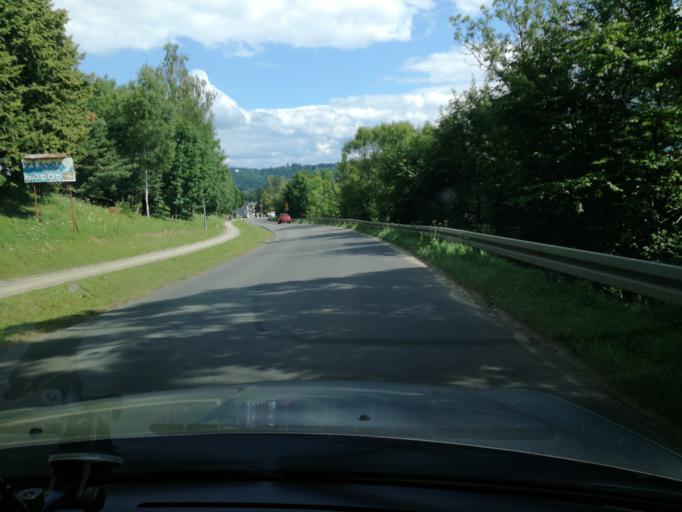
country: PL
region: Subcarpathian Voivodeship
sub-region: Powiat leski
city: Polanczyk
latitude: 49.3660
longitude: 22.4230
